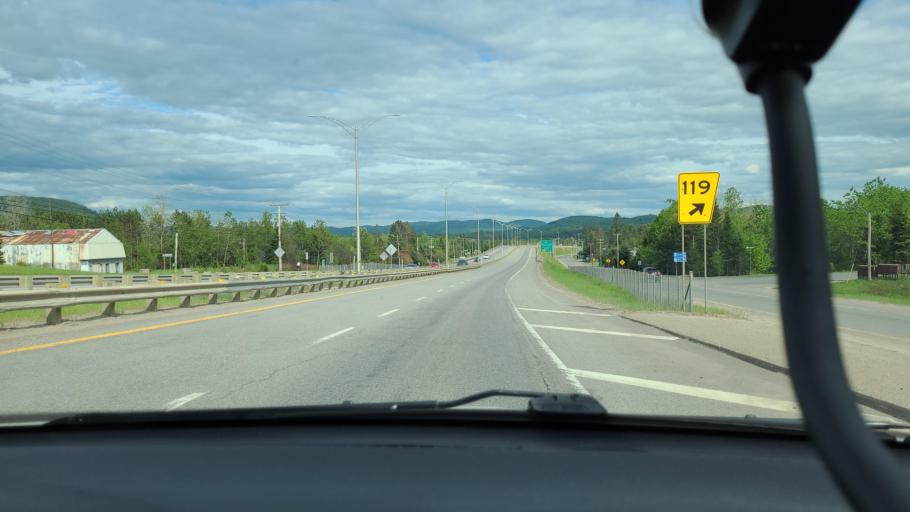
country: CA
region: Quebec
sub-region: Laurentides
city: Mont-Tremblant
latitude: 46.1344
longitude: -74.6193
